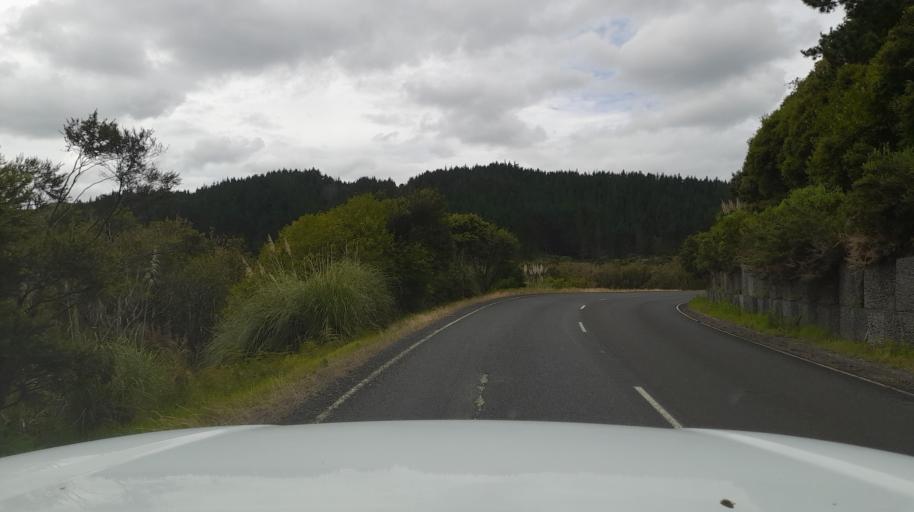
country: NZ
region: Northland
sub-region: Far North District
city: Kaitaia
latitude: -35.3635
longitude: 173.4341
